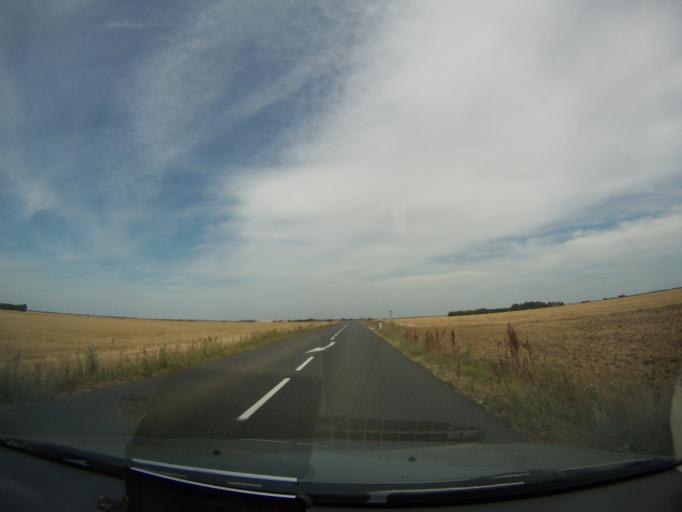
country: FR
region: Poitou-Charentes
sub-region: Departement des Deux-Sevres
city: Airvault
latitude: 46.8114
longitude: -0.0612
